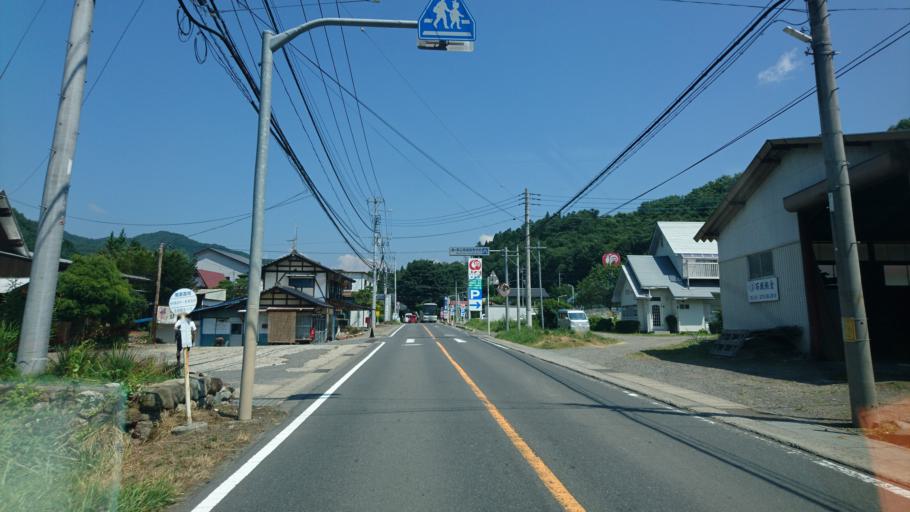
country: JP
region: Gunma
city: Numata
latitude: 36.7301
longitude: 139.2251
